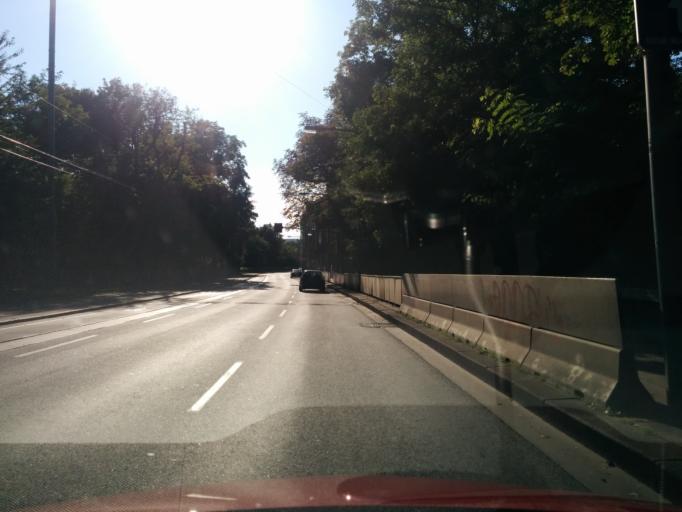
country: AT
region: Vienna
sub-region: Wien Stadt
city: Vienna
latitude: 48.1882
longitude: 16.3125
